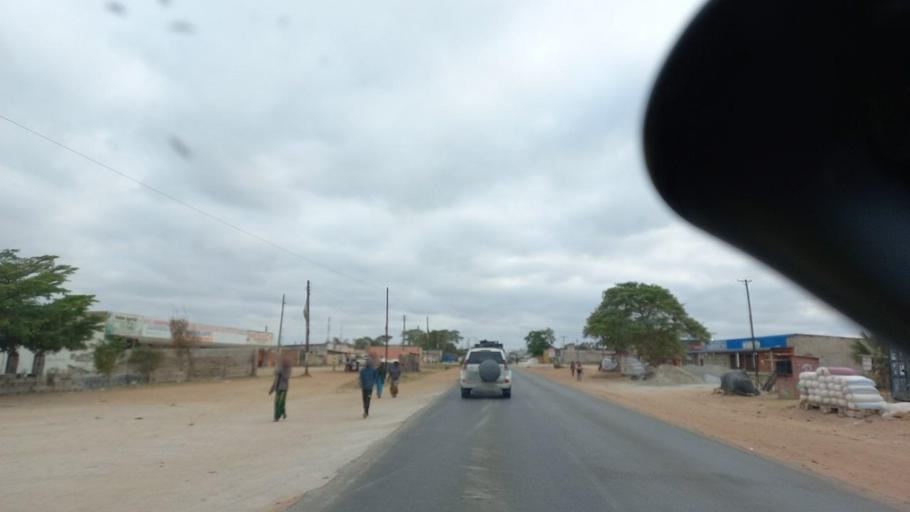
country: ZM
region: Lusaka
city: Chongwe
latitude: -15.3345
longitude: 28.6716
